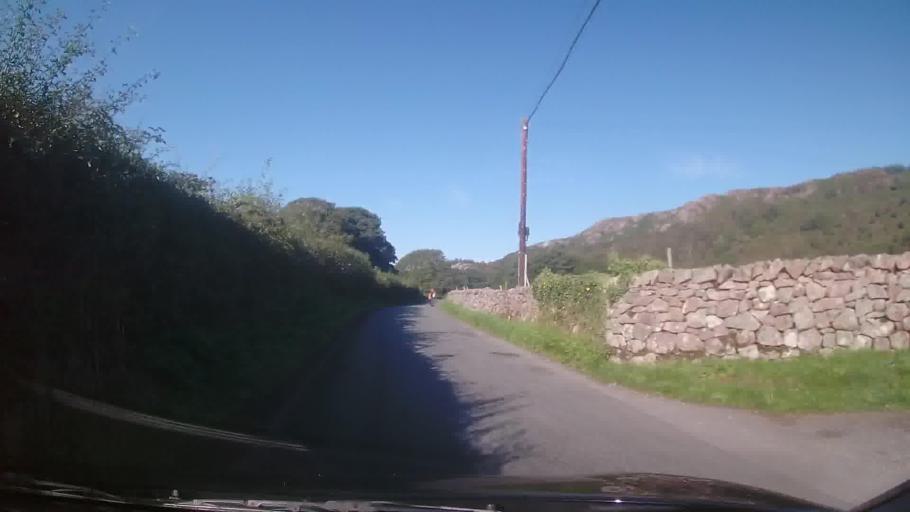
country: GB
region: England
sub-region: Cumbria
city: Seascale
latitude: 54.3906
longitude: -3.2988
